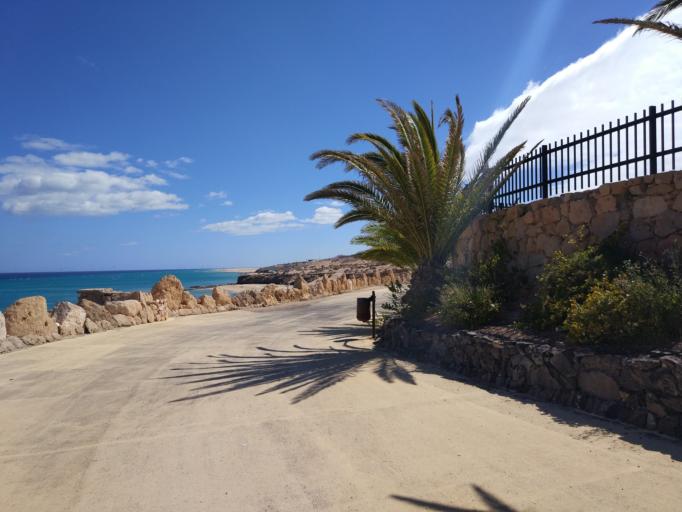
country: ES
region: Canary Islands
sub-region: Provincia de Las Palmas
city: Pajara
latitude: 28.1483
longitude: -14.2322
